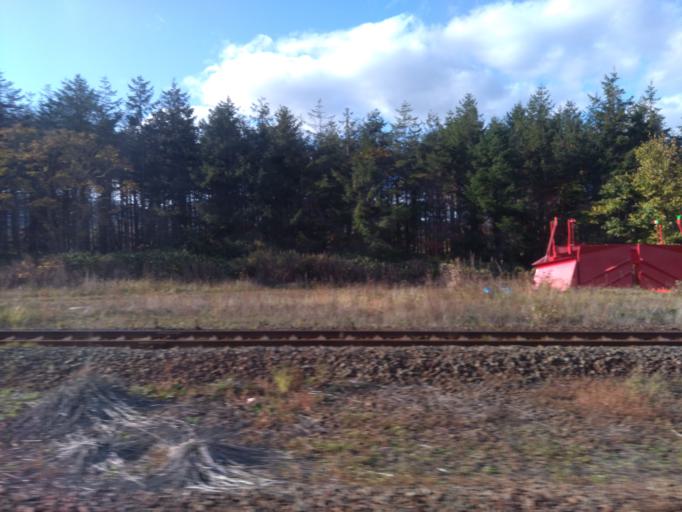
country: JP
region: Hokkaido
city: Niseko Town
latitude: 42.5825
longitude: 140.4582
